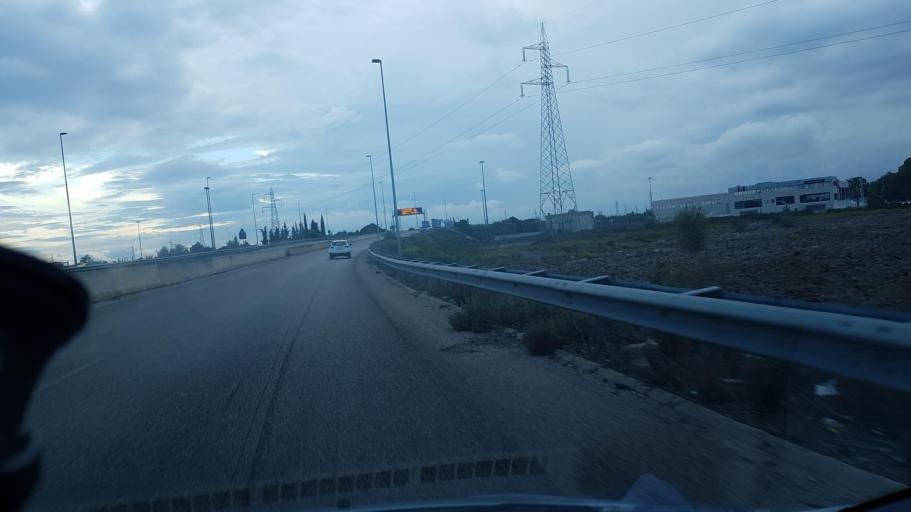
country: IT
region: Apulia
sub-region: Provincia di Lecce
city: Giorgilorio
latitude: 40.3756
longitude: 18.1509
